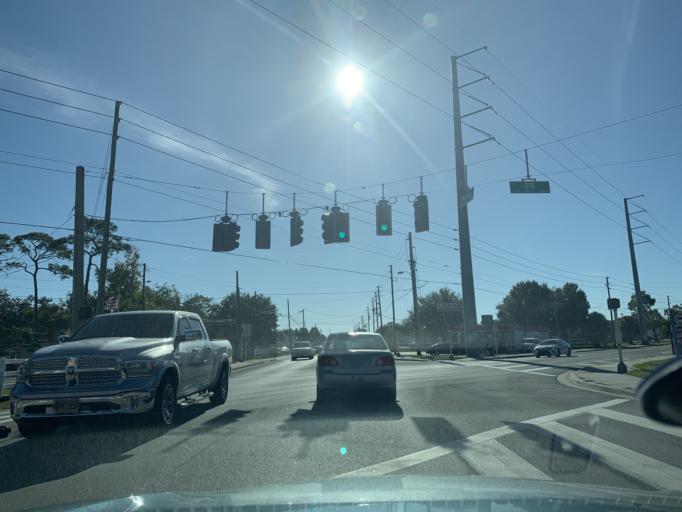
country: US
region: Florida
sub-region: Pinellas County
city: Lealman
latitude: 27.8240
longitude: -82.6715
